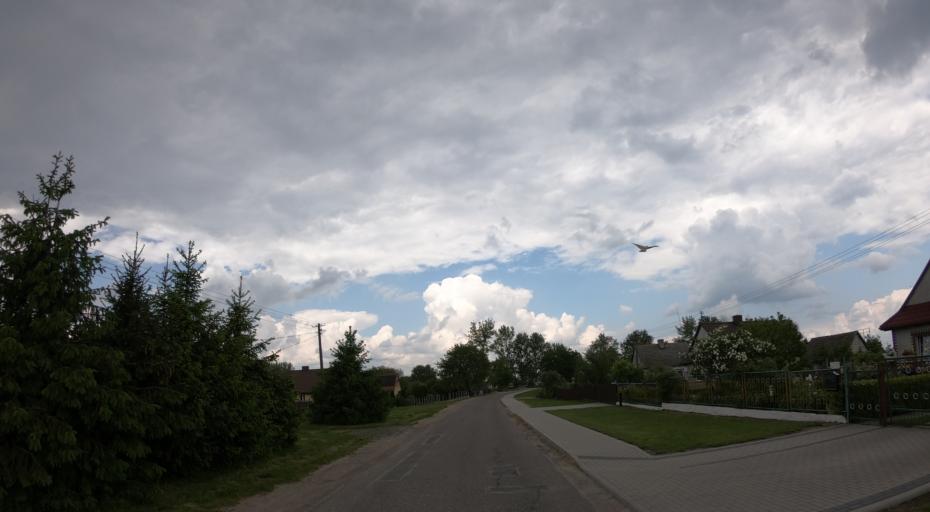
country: PL
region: West Pomeranian Voivodeship
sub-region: Powiat pyrzycki
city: Bielice
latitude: 53.2014
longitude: 14.7684
